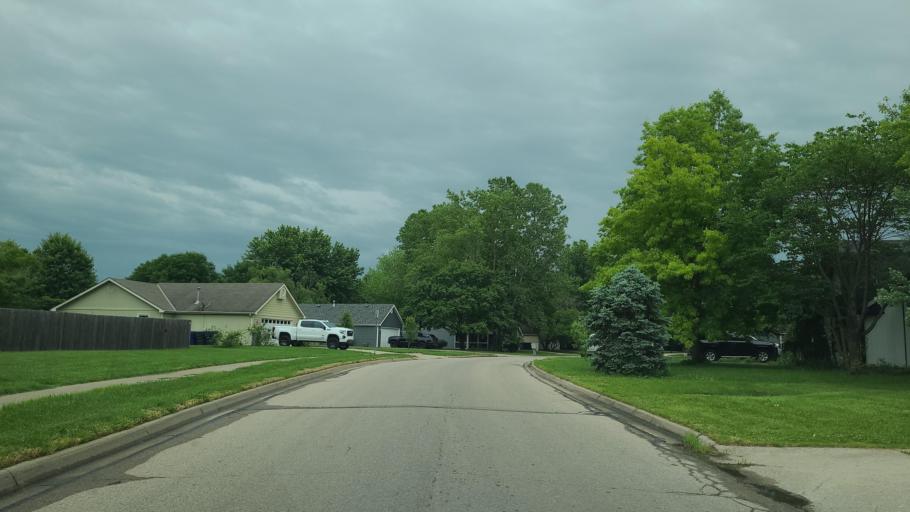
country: US
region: Kansas
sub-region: Douglas County
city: Lawrence
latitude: 38.9332
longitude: -95.2818
